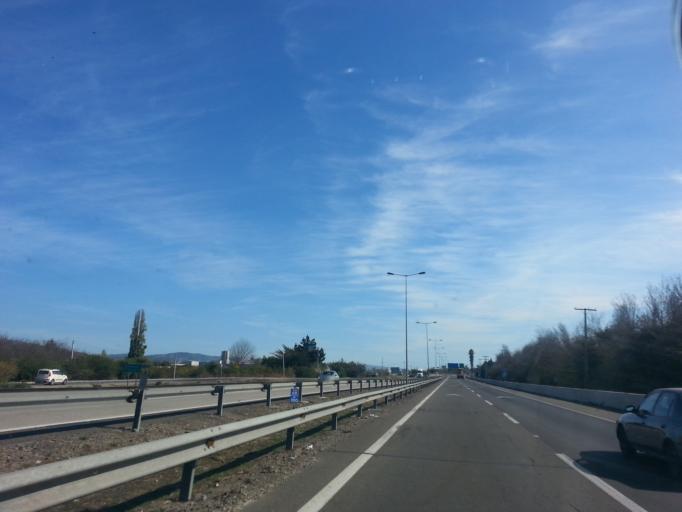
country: CL
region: Valparaiso
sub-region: Provincia de Marga Marga
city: Villa Alemana
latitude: -33.3333
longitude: -71.3823
